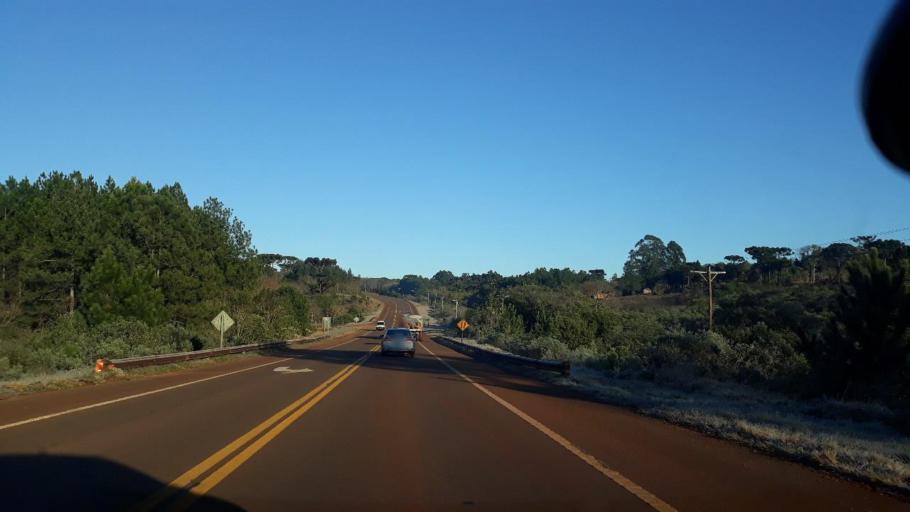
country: AR
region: Misiones
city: San Vicente
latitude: -26.6368
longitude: -54.1319
